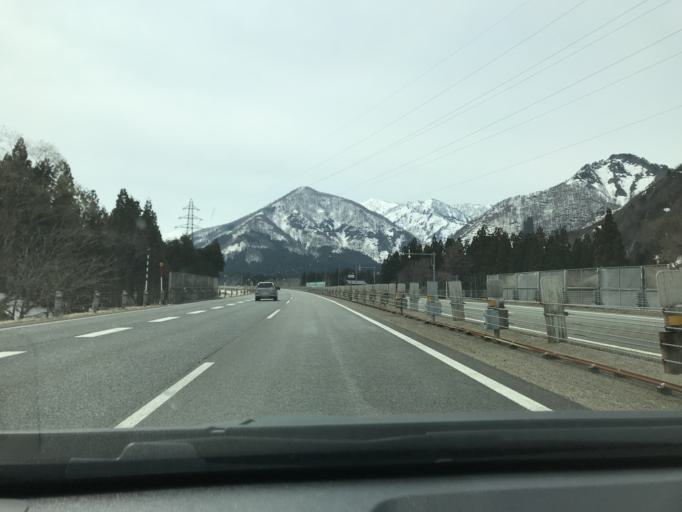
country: JP
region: Niigata
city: Shiozawa
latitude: 36.9200
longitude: 138.8431
